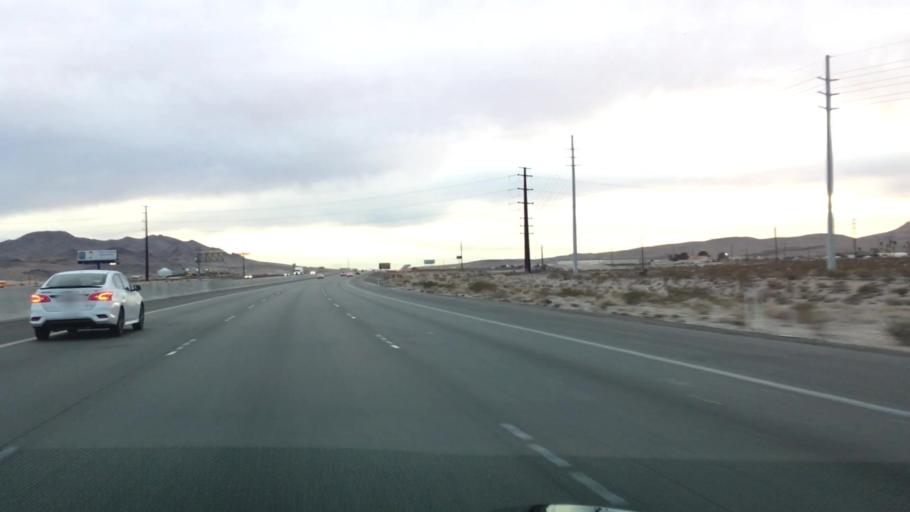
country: US
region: Nevada
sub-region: Clark County
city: Enterprise
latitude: 35.9422
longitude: -115.1855
